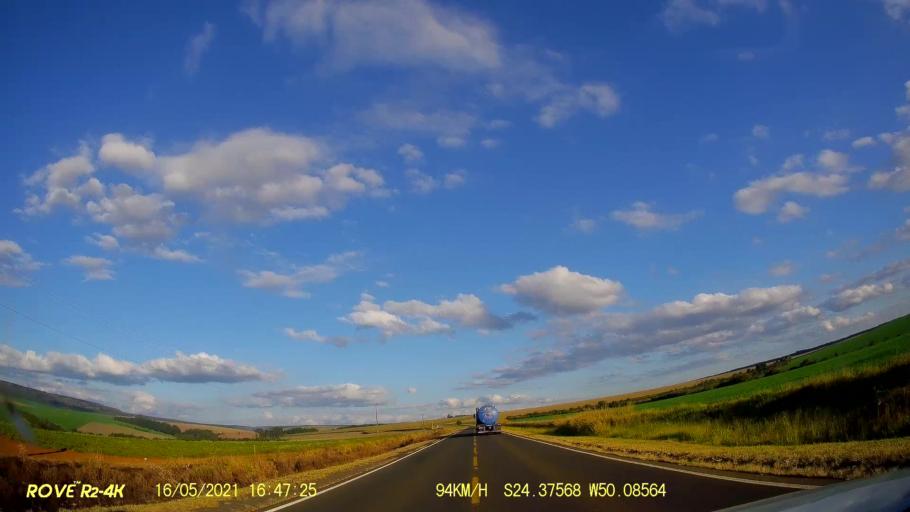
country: BR
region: Parana
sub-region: Pirai Do Sul
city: Pirai do Sul
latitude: -24.3760
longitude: -50.0857
